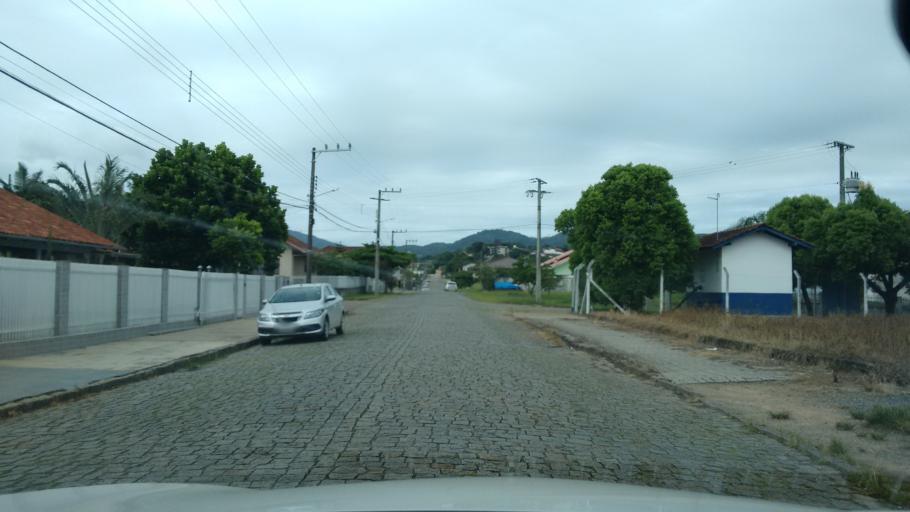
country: BR
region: Santa Catarina
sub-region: Timbo
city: Timbo
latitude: -26.8136
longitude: -49.2713
